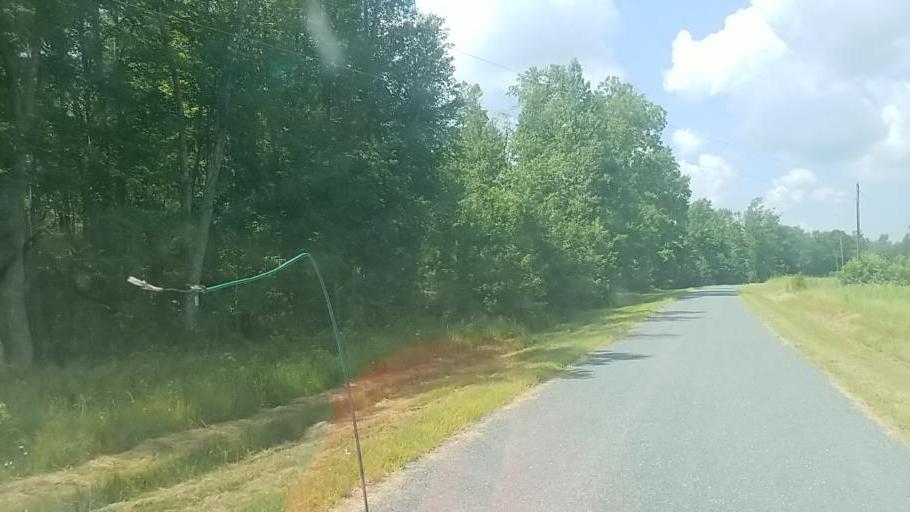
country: US
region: Maryland
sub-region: Worcester County
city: Snow Hill
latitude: 38.2501
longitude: -75.4244
